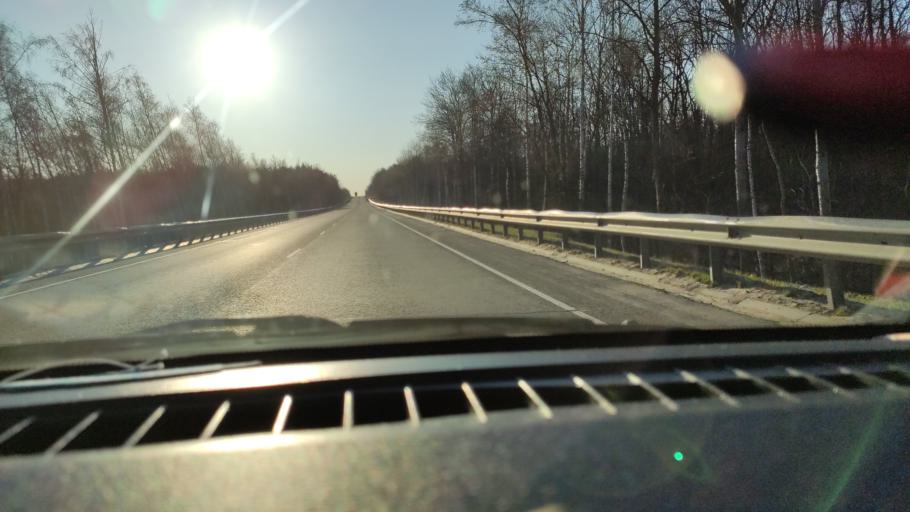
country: RU
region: Saratov
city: Vol'sk
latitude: 52.1109
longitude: 47.3458
